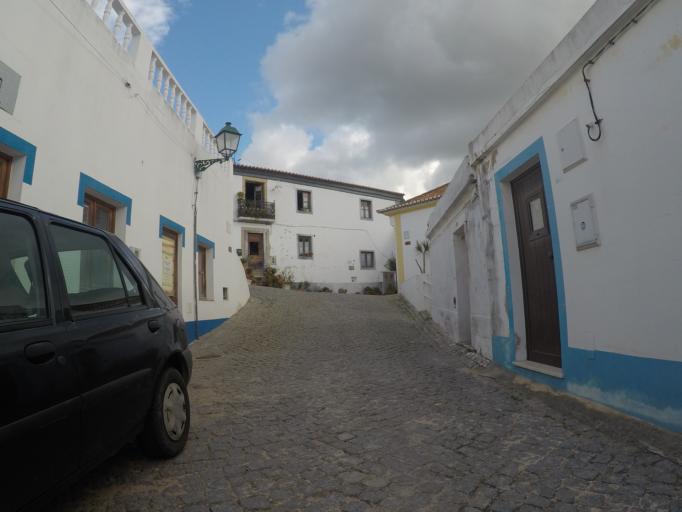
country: PT
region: Faro
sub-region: Aljezur
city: Aljezur
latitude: 37.3191
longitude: -8.8030
